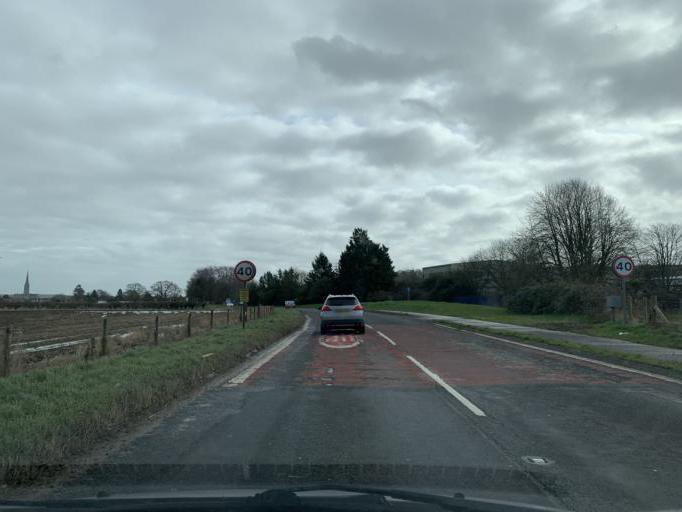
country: GB
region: England
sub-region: Wiltshire
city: Salisbury
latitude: 51.0624
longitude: -1.8274
